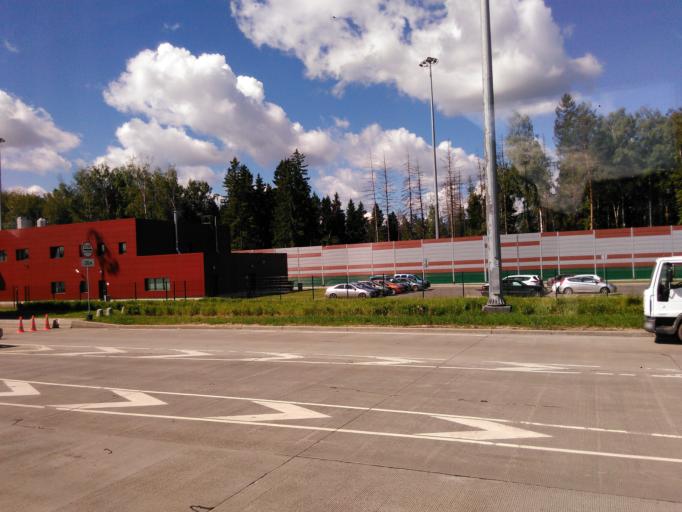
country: RU
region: Moscow
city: Khimki
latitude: 55.9358
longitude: 37.4487
